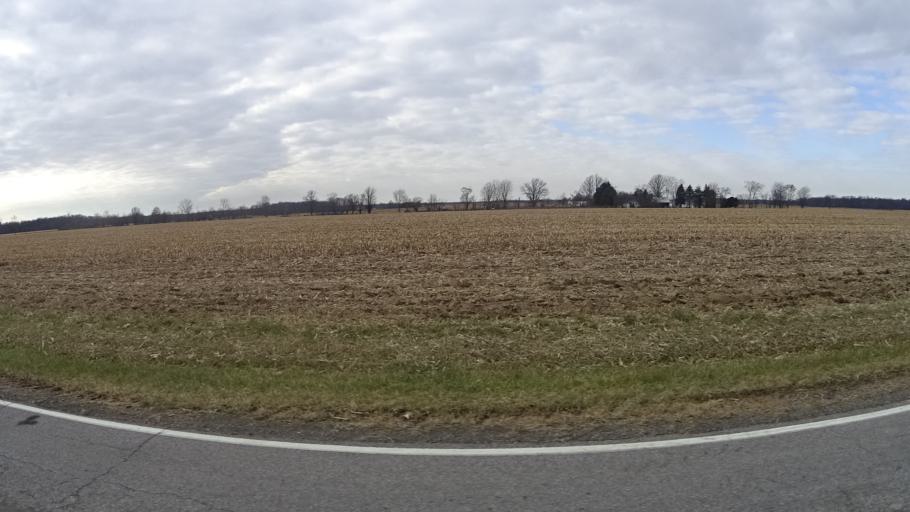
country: US
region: Ohio
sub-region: Lorain County
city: Camden
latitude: 41.2359
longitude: -82.3368
